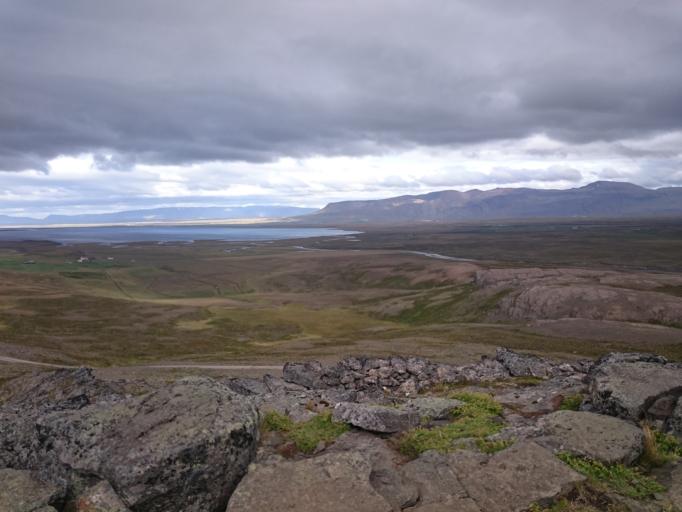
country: IS
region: Northwest
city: Saudarkrokur
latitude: 65.4752
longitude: -20.5966
